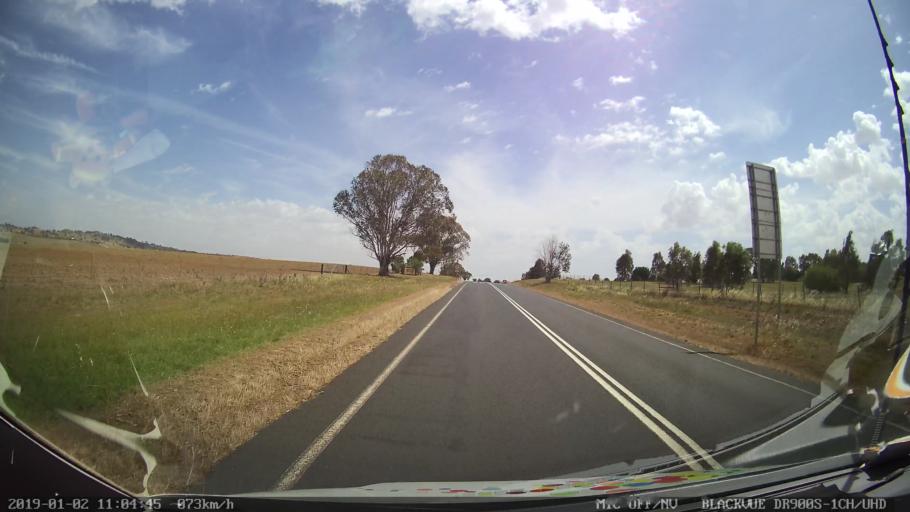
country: AU
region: New South Wales
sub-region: Young
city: Young
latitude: -34.5731
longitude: 148.3538
